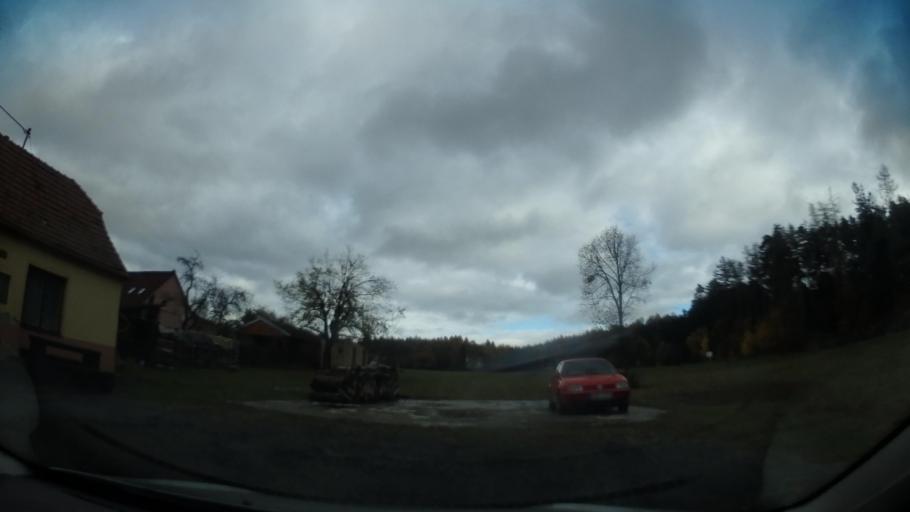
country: CZ
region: Vysocina
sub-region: Okres Zd'ar nad Sazavou
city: Velka Bites
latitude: 49.2537
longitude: 16.2586
